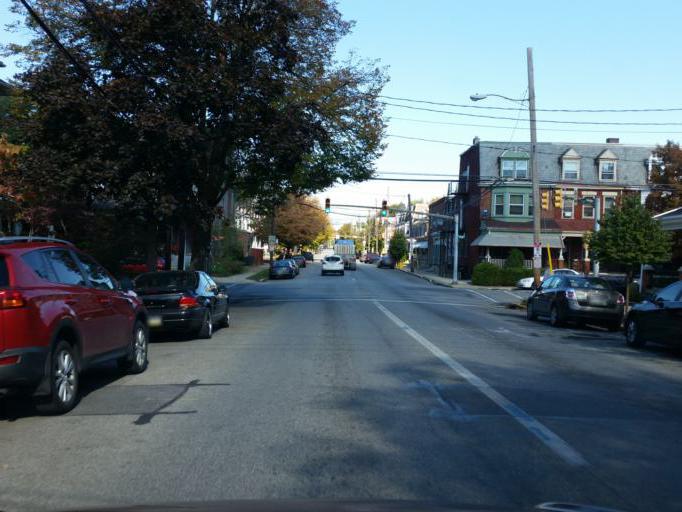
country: US
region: Pennsylvania
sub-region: Lancaster County
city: Lancaster
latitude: 40.0499
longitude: -76.3035
